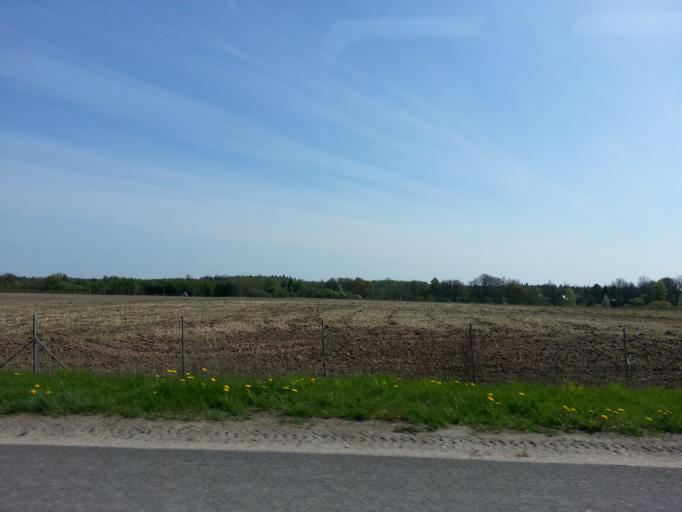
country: LT
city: Sirvintos
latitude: 55.0826
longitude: 24.8741
